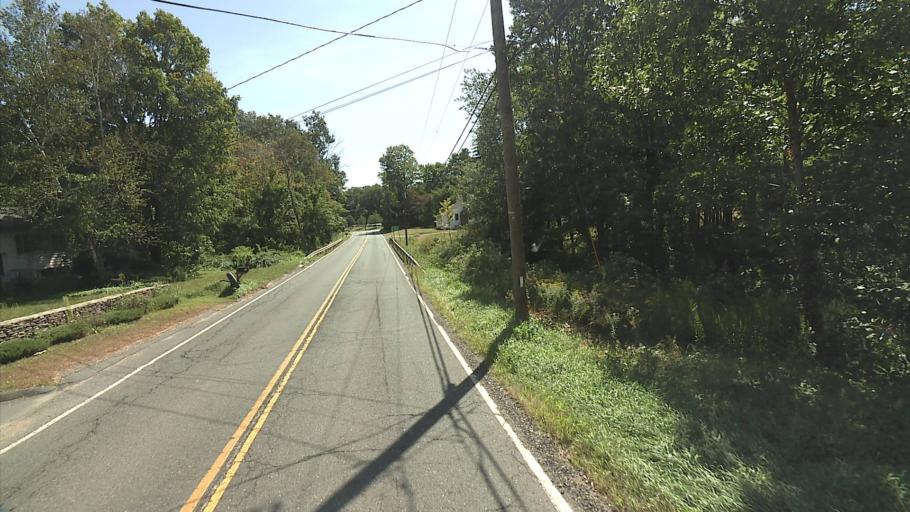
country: US
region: Connecticut
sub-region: New Haven County
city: Southbury
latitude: 41.4663
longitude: -73.1626
